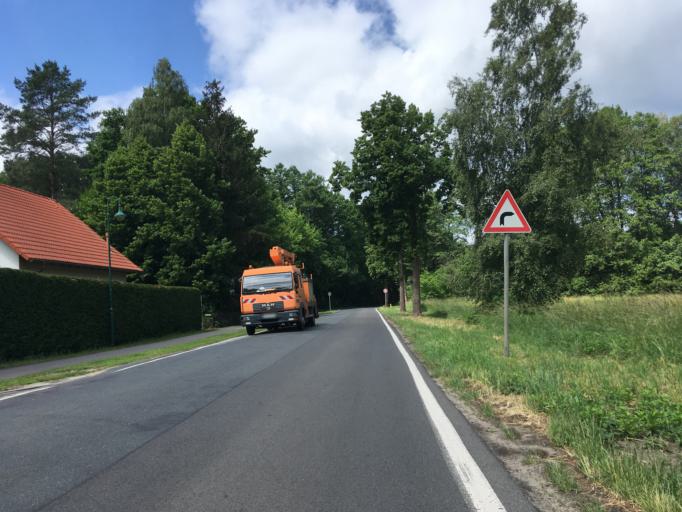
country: DE
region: Brandenburg
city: Wandlitz
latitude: 52.7708
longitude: 13.4527
